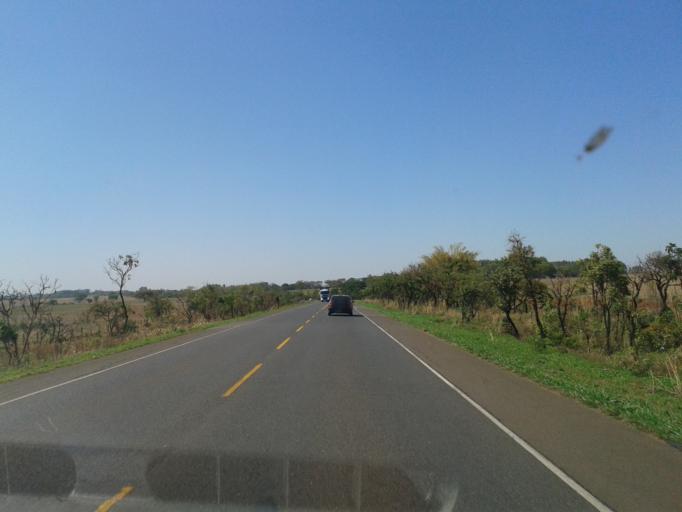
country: BR
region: Minas Gerais
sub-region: Uberlandia
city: Uberlandia
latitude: -19.0314
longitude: -48.0668
